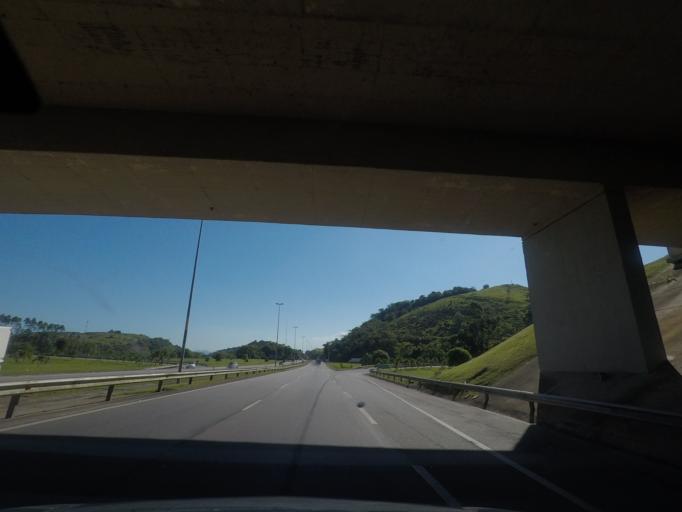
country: BR
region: Rio de Janeiro
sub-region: Guapimirim
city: Guapimirim
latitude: -22.6562
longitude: -43.0883
